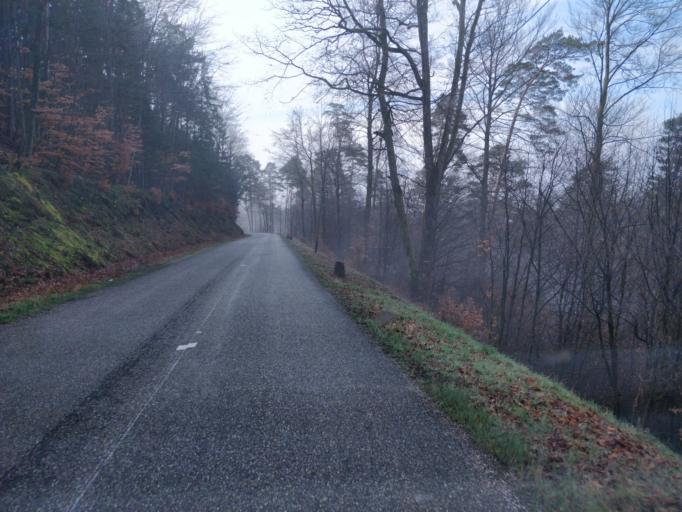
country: FR
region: Lorraine
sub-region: Departement de la Moselle
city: Soucht
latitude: 48.9351
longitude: 7.3654
